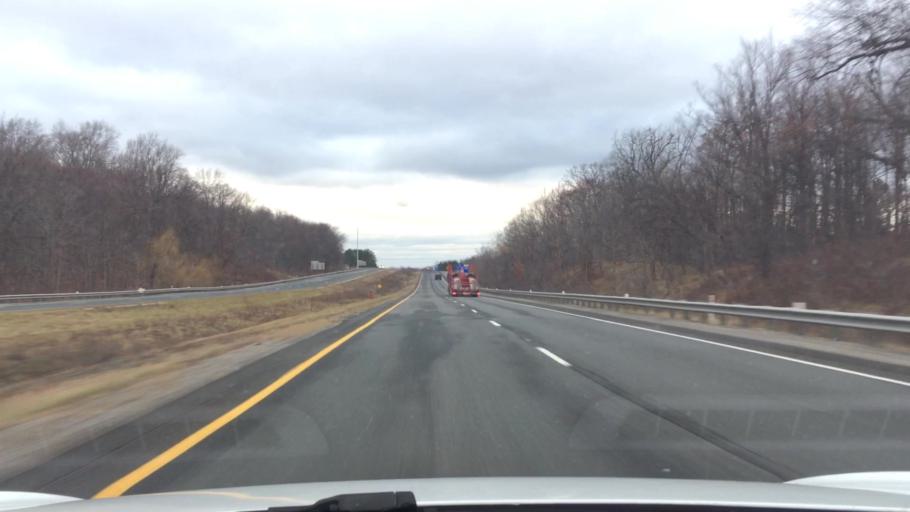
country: CA
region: Ontario
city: Niagara Falls
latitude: 43.1508
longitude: -79.1168
